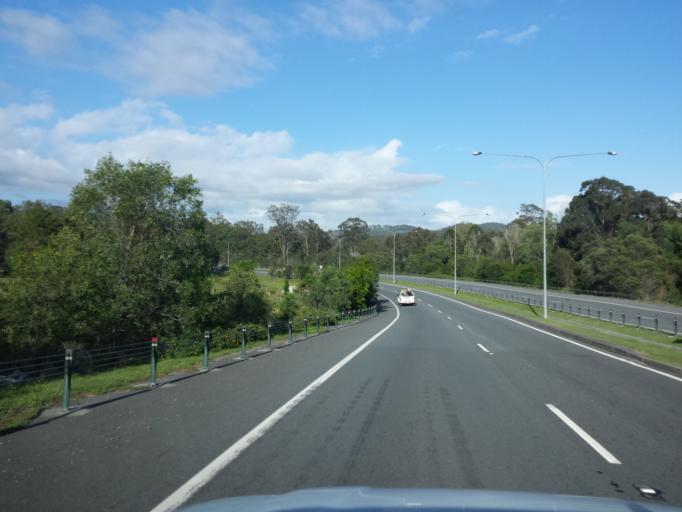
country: AU
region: Queensland
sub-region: Logan
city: Windaroo
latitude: -27.7718
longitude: 153.2054
